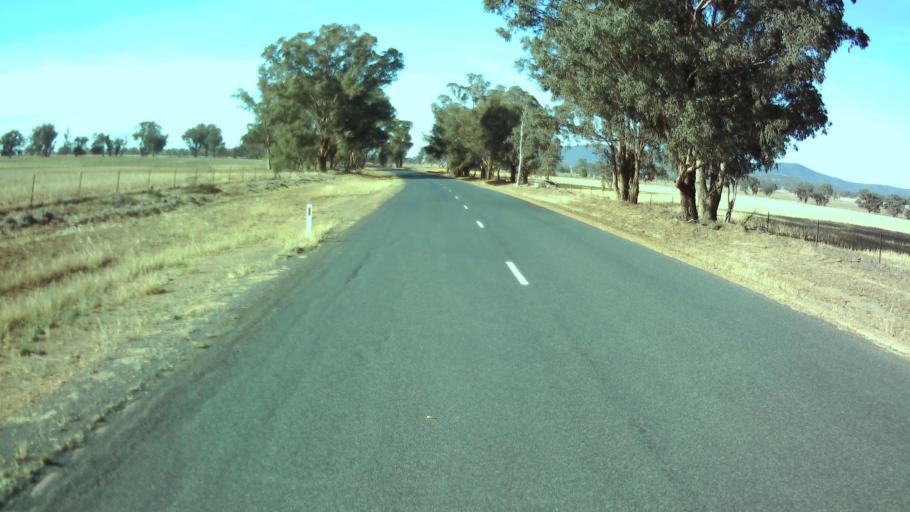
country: AU
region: New South Wales
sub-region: Weddin
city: Grenfell
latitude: -33.9237
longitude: 148.1390
